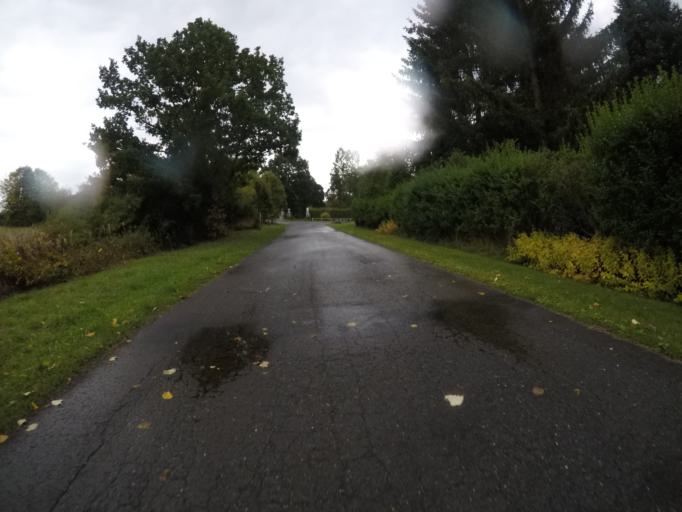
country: BE
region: Wallonia
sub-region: Province du Luxembourg
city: Martelange
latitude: 49.8468
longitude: 5.7054
